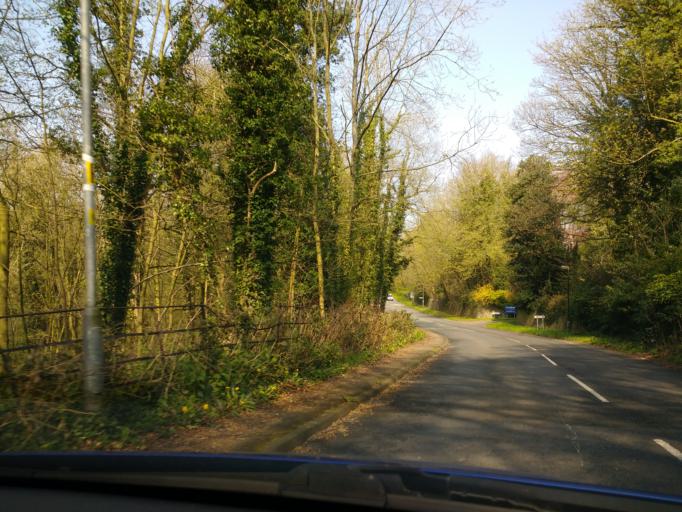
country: GB
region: England
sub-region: Lancashire
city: Bolton le Sands
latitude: 54.0778
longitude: -2.7667
